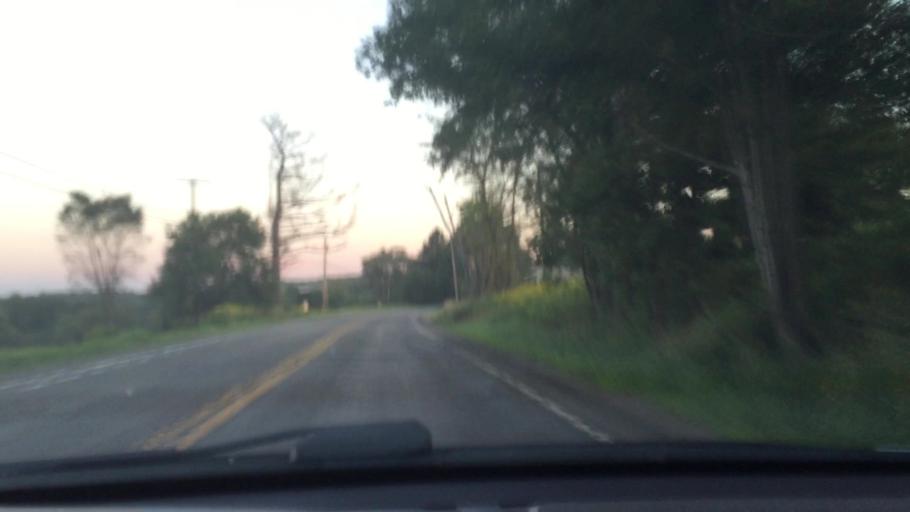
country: US
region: Pennsylvania
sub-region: Butler County
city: Slippery Rock
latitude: 41.1005
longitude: -80.0520
